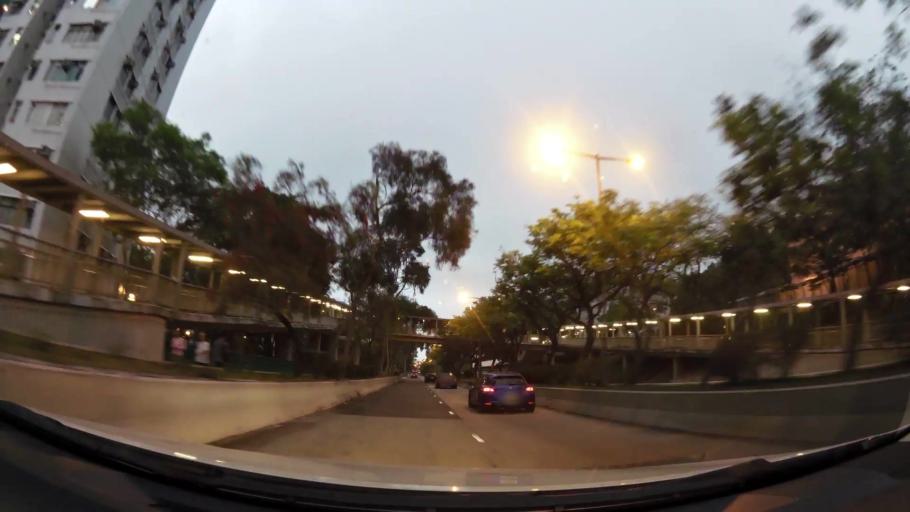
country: HK
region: Tsuen Wan
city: Tsuen Wan
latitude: 22.3494
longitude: 114.1024
